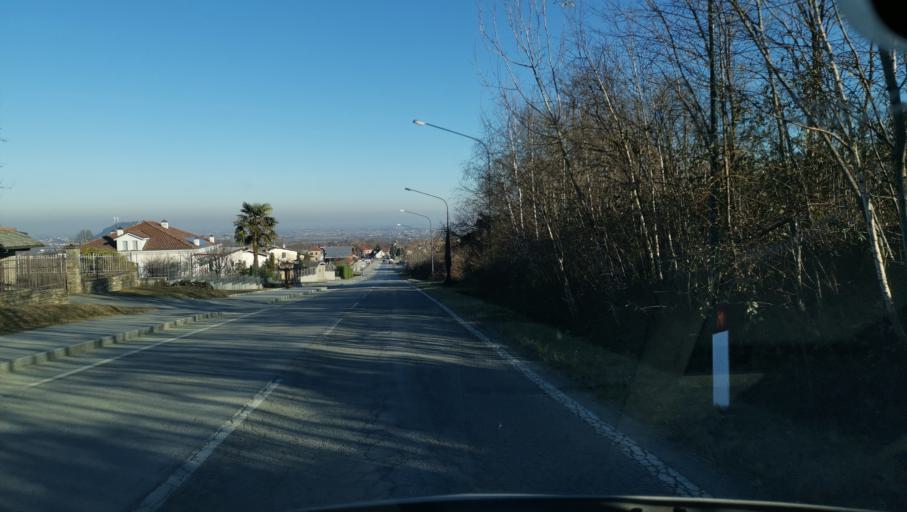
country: IT
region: Piedmont
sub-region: Provincia di Cuneo
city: Bagnolo Piemonte
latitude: 44.7532
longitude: 7.2983
